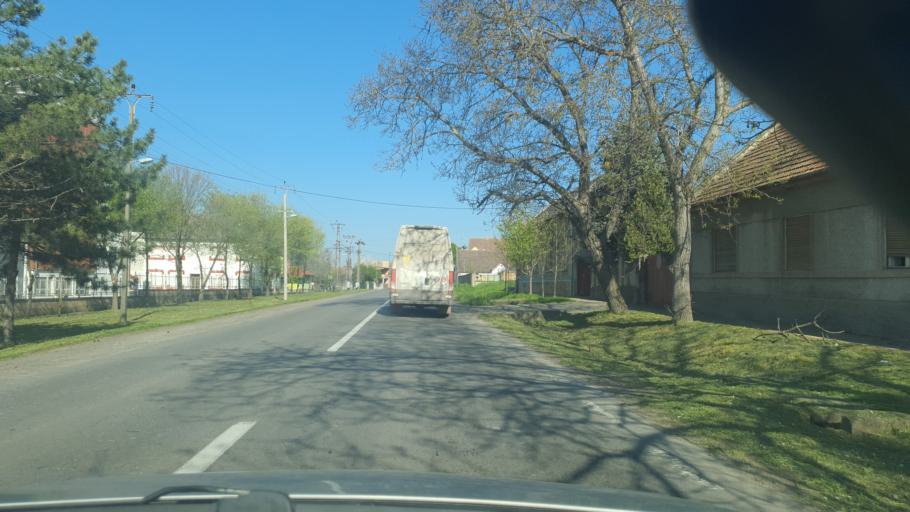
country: RS
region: Autonomna Pokrajina Vojvodina
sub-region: Zapadnobacki Okrug
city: Kula
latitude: 45.6917
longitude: 19.3828
